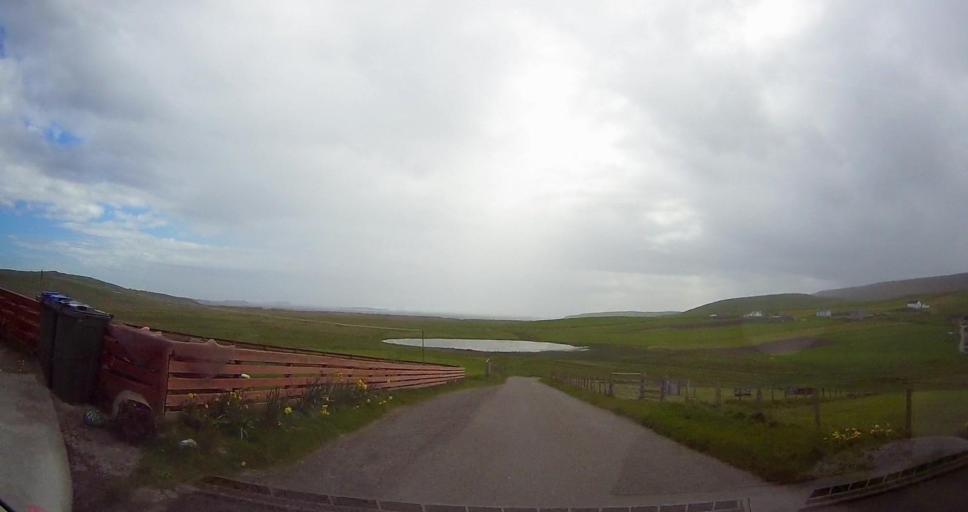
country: GB
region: Scotland
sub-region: Shetland Islands
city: Sandwick
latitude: 59.9119
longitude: -1.3272
